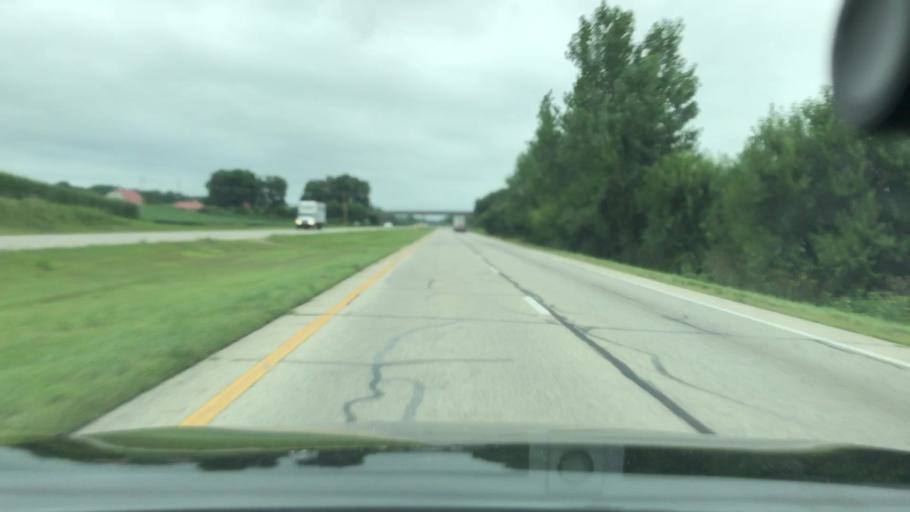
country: US
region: Ohio
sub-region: Ross County
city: Kingston
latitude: 39.4821
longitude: -82.9714
